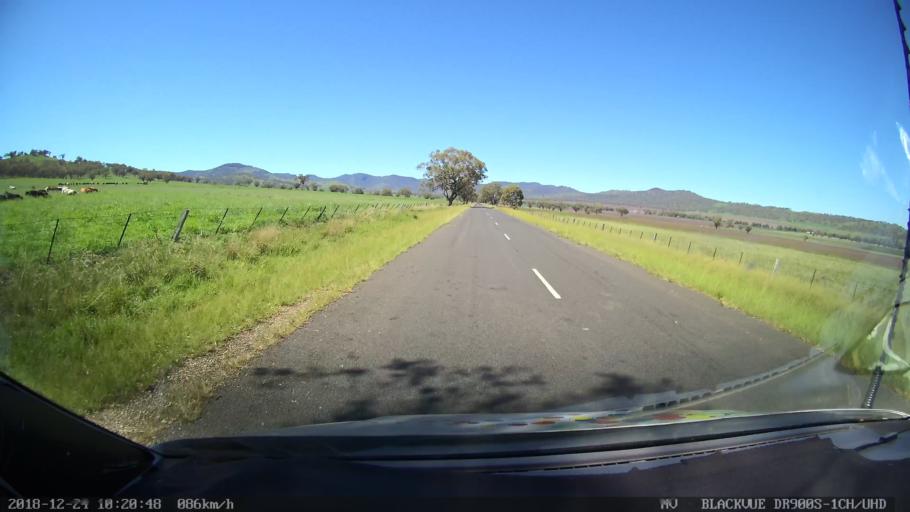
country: AU
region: New South Wales
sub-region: Liverpool Plains
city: Quirindi
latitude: -31.7449
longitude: 150.5549
